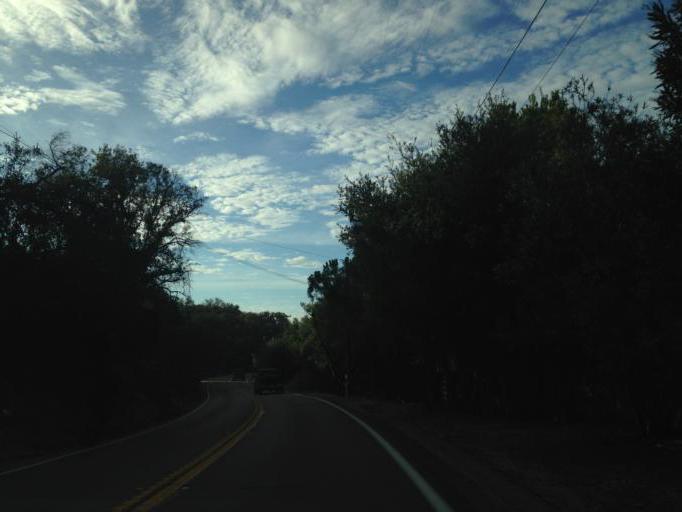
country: US
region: California
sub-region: San Diego County
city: Rainbow
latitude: 33.4276
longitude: -117.0890
